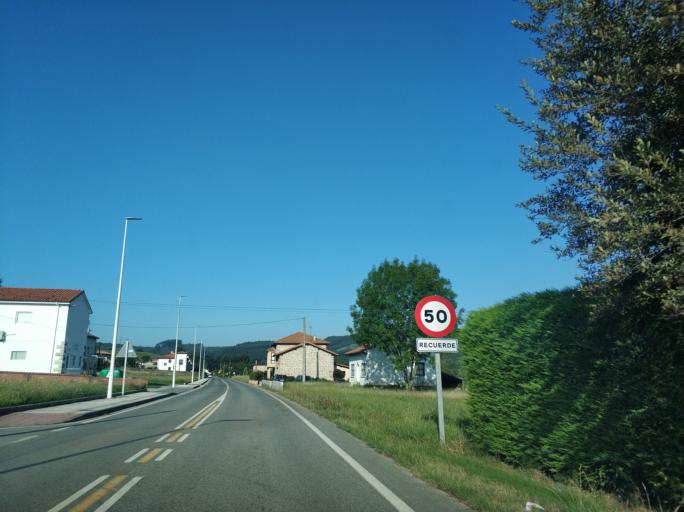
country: ES
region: Cantabria
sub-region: Provincia de Cantabria
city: Miengo
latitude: 43.3903
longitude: -3.9526
